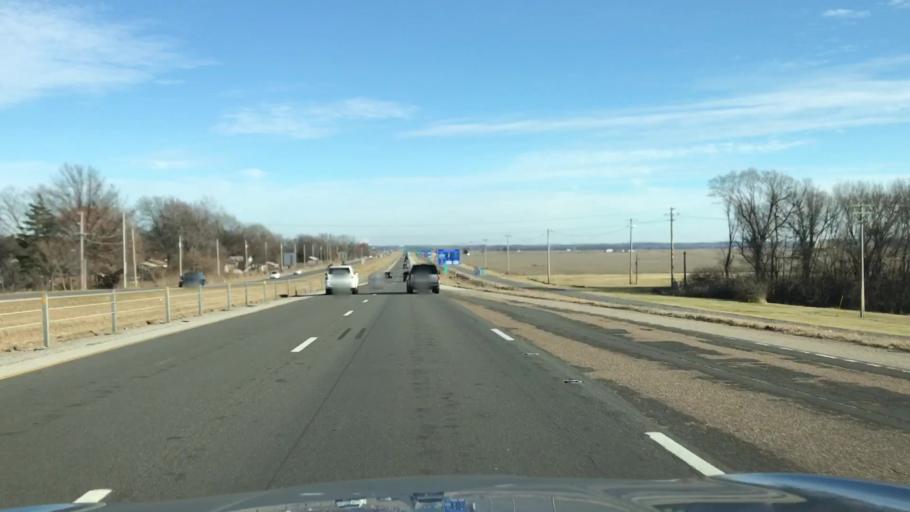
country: US
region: Illinois
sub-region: Madison County
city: Mitchell
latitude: 38.7577
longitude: -90.0868
